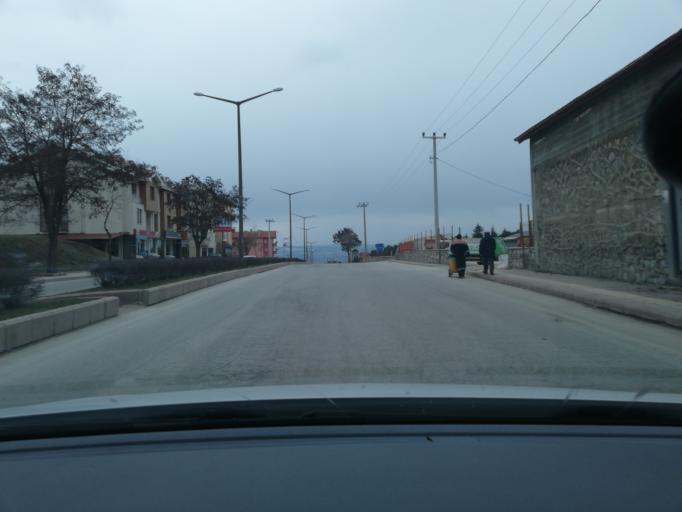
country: TR
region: Bolu
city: Gerede
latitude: 40.7957
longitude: 32.2053
